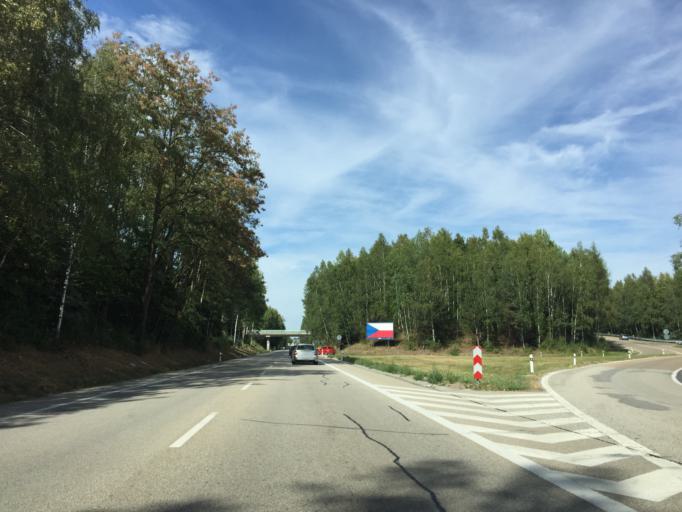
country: CZ
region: Central Bohemia
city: Votice
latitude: 49.6593
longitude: 14.6341
